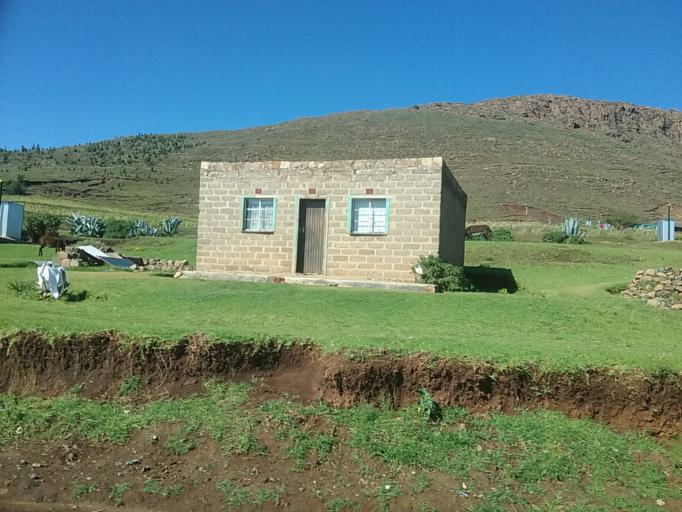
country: LS
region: Berea
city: Teyateyaneng
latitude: -29.2301
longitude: 27.8783
